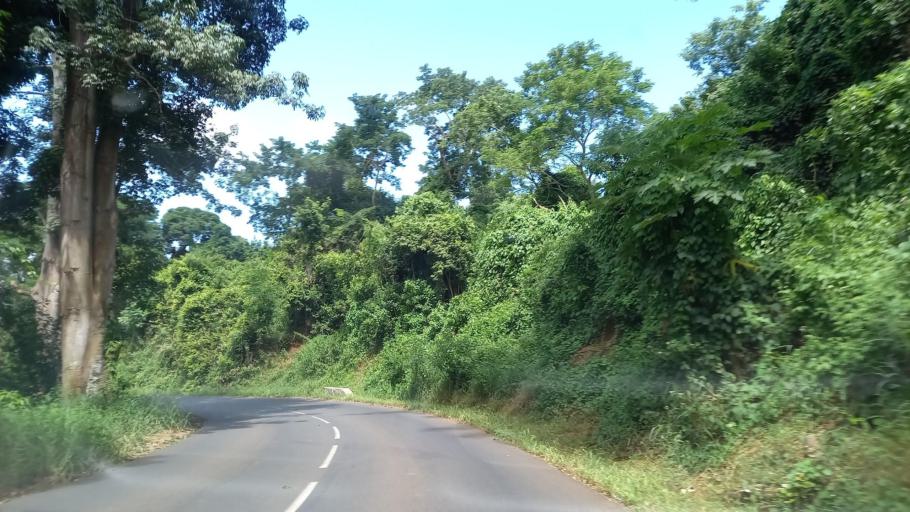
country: YT
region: Acoua
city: Acoua
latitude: -12.7466
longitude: 45.0551
